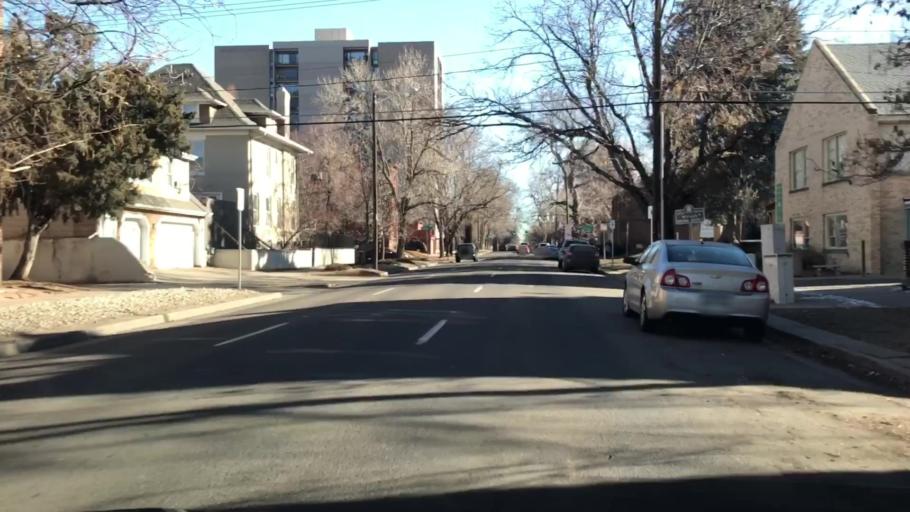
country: US
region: Colorado
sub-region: Denver County
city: Denver
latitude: 39.7384
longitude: -104.9681
